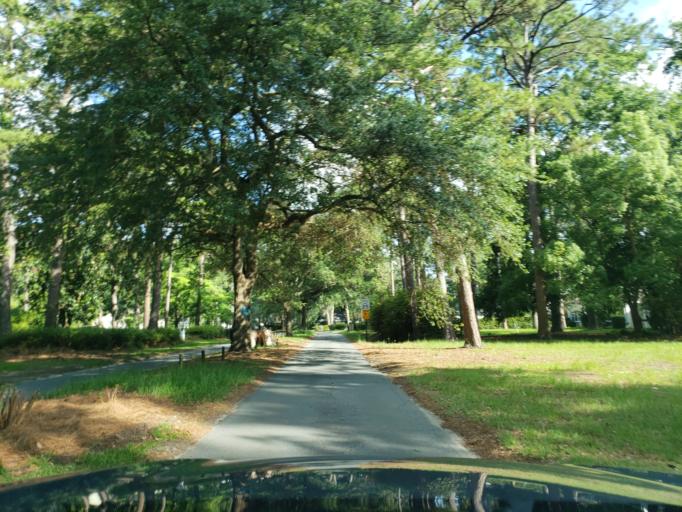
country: US
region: Georgia
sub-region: Chatham County
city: Isle of Hope
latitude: 31.9778
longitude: -81.0619
